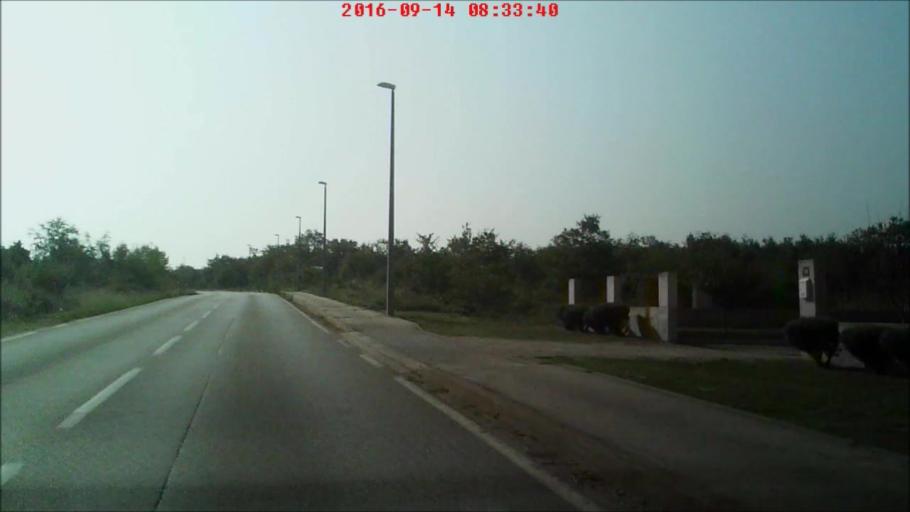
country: HR
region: Zadarska
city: Policnik
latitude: 44.1548
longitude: 15.3139
